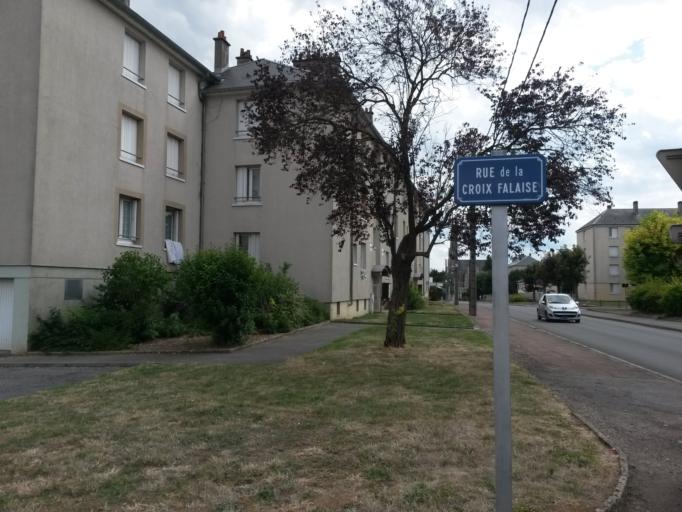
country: FR
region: Centre
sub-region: Departement du Loiret
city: Pithiviers
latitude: 48.1790
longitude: 2.2563
